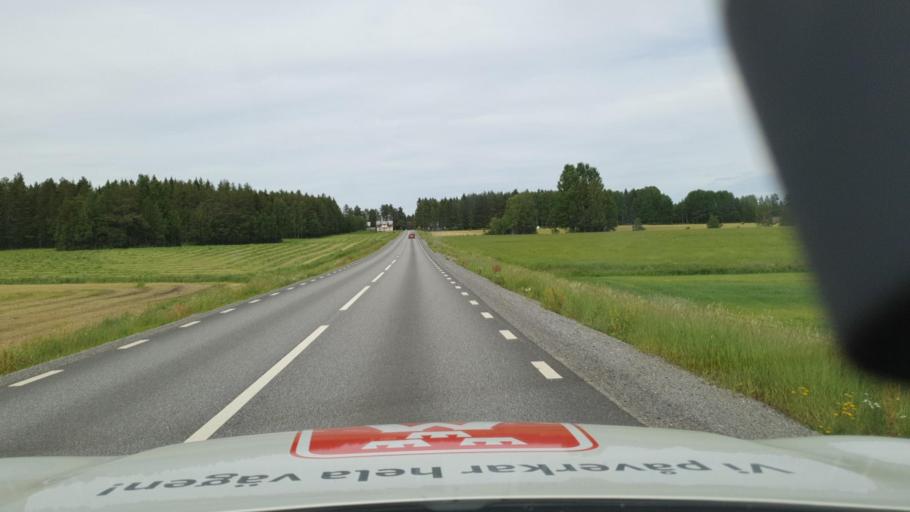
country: SE
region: Vaesterbotten
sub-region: Skelleftea Kommun
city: Burtraesk
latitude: 64.5068
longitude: 20.6295
